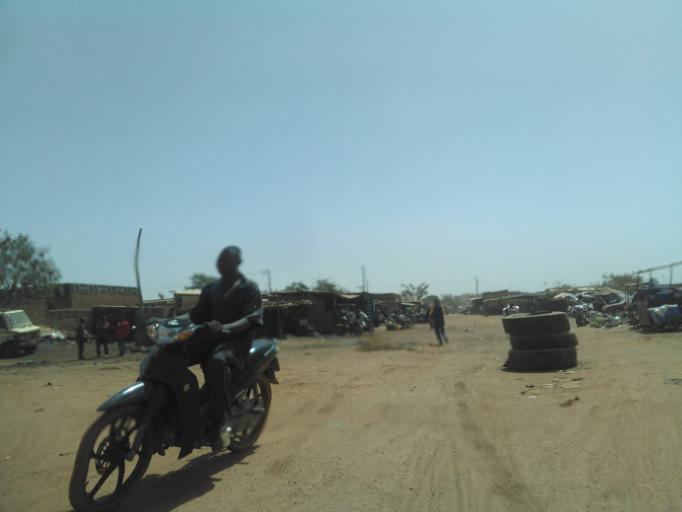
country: BF
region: Centre
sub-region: Kadiogo Province
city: Ouagadougou
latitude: 12.3913
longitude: -1.5660
